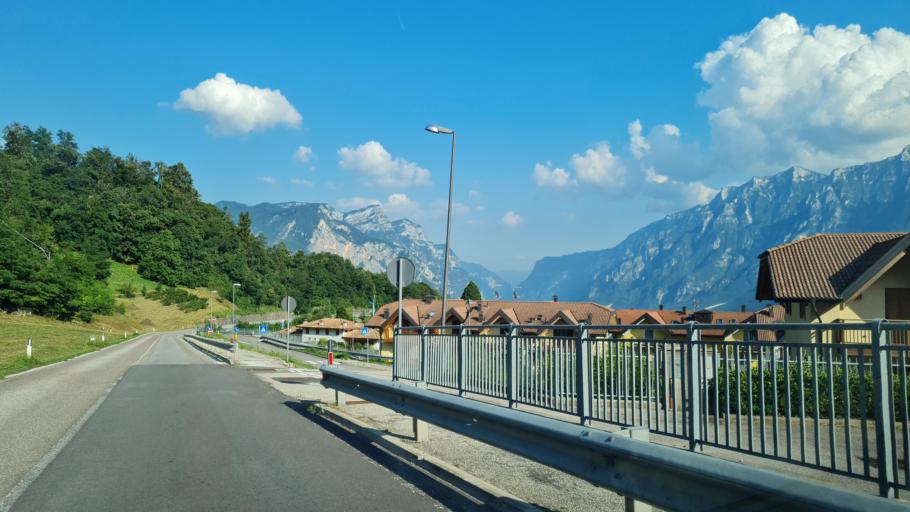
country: IT
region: Trentino-Alto Adige
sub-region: Provincia di Trento
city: Telve di Sopra
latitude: 46.0749
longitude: 11.4765
